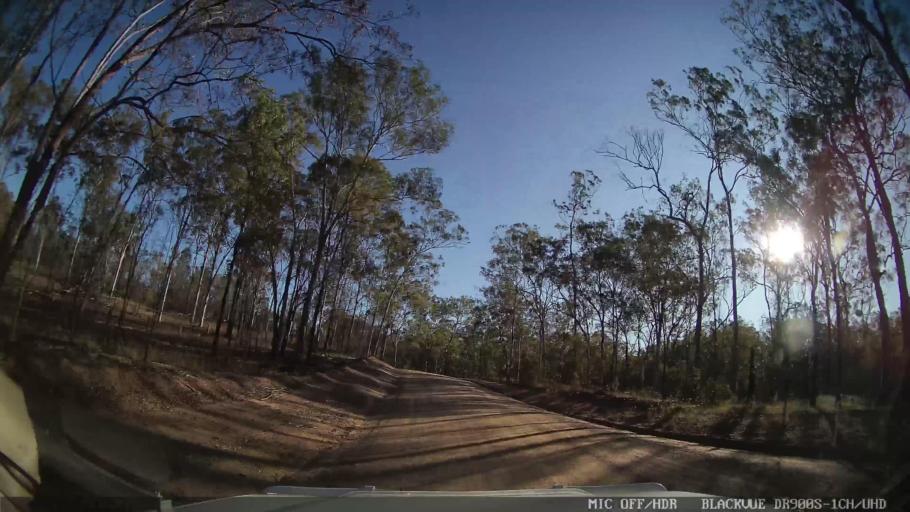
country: AU
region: Queensland
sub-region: Bundaberg
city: Sharon
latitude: -24.7360
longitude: 151.5216
